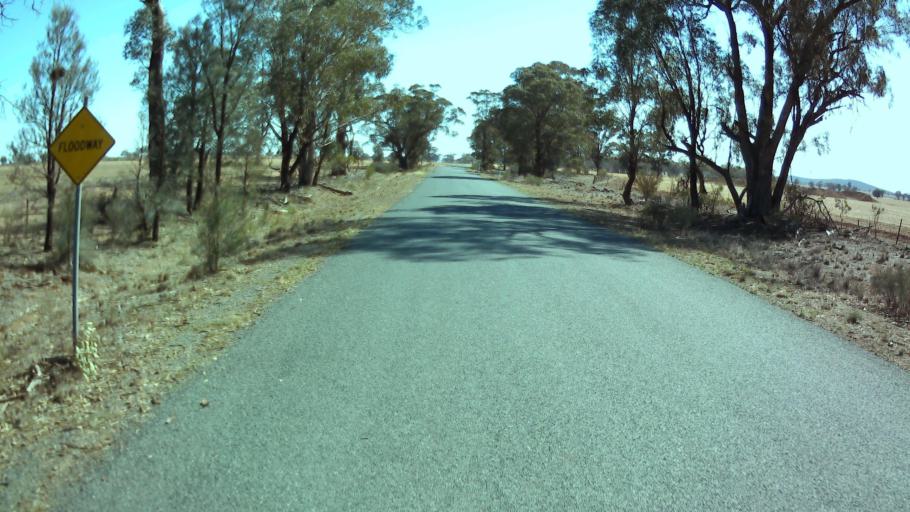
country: AU
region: New South Wales
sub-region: Weddin
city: Grenfell
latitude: -33.7384
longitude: 147.8829
